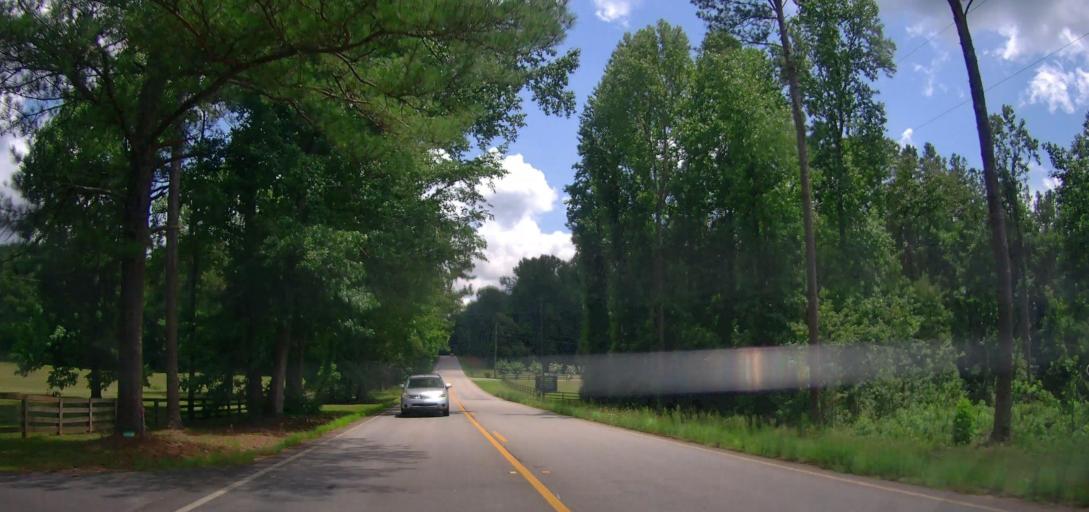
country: US
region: Georgia
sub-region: Troup County
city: Hogansville
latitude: 33.1342
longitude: -84.8338
